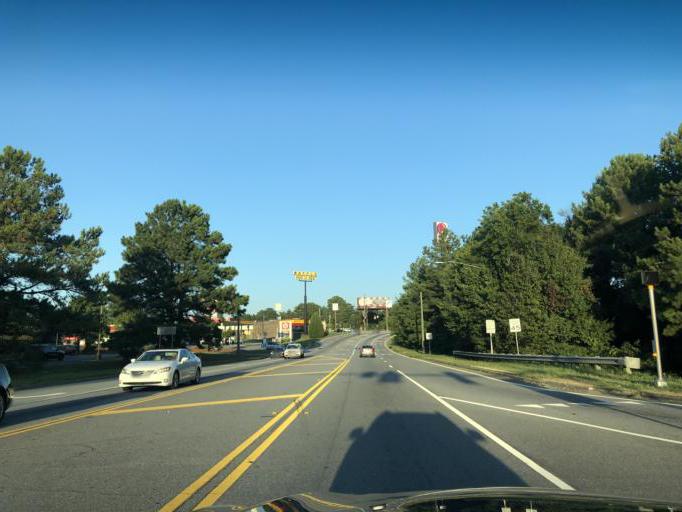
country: US
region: Georgia
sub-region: Muscogee County
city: Columbus
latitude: 32.5224
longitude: -84.8908
